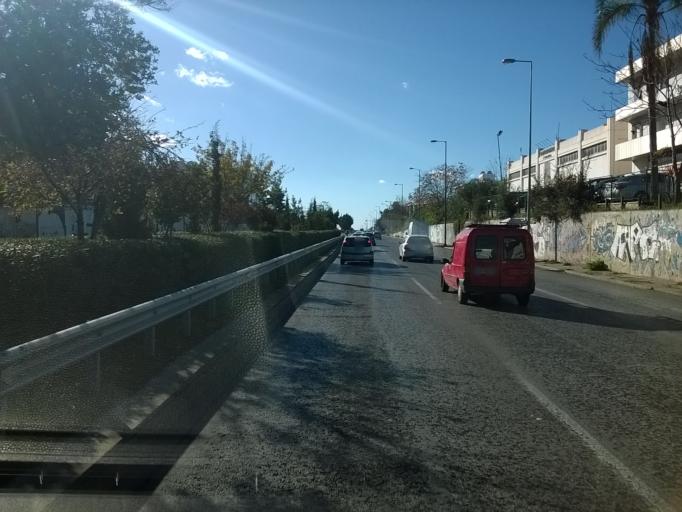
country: GR
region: Attica
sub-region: Nomarchia Athinas
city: Agios Dimitrios
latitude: 37.9265
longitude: 23.7443
